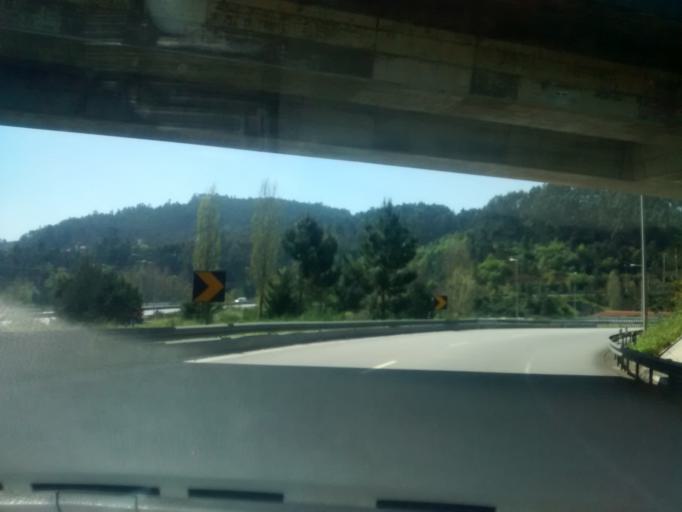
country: PT
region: Braga
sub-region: Braga
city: Oliveira
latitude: 41.5095
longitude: -8.4451
